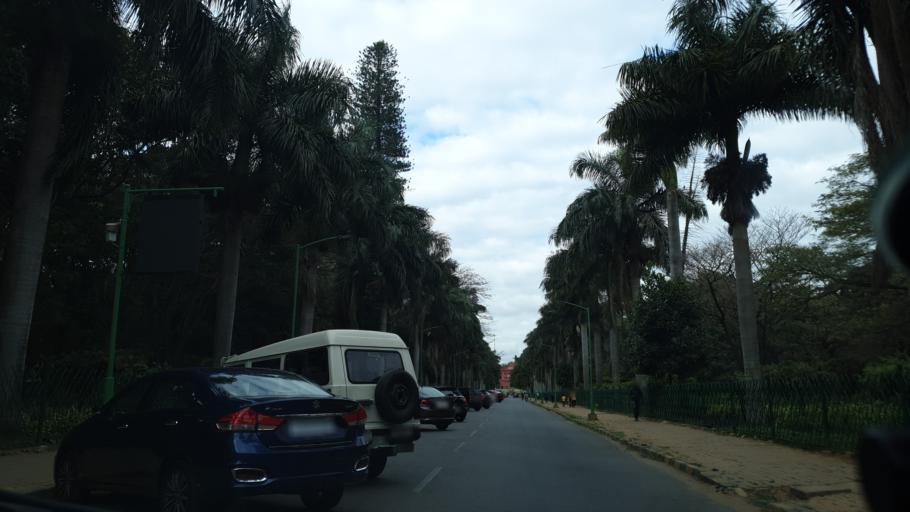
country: IN
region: Karnataka
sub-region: Bangalore Urban
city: Bangalore
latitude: 12.9694
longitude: 77.5892
